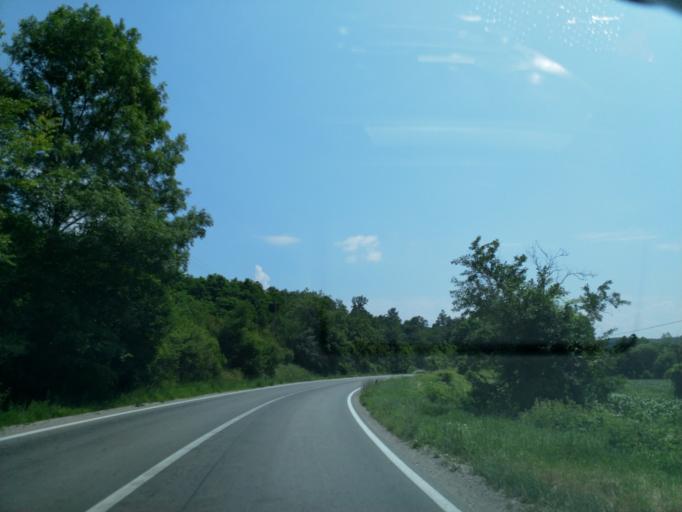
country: RS
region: Central Serbia
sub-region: Toplicki Okrug
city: Blace
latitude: 43.3316
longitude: 21.2173
